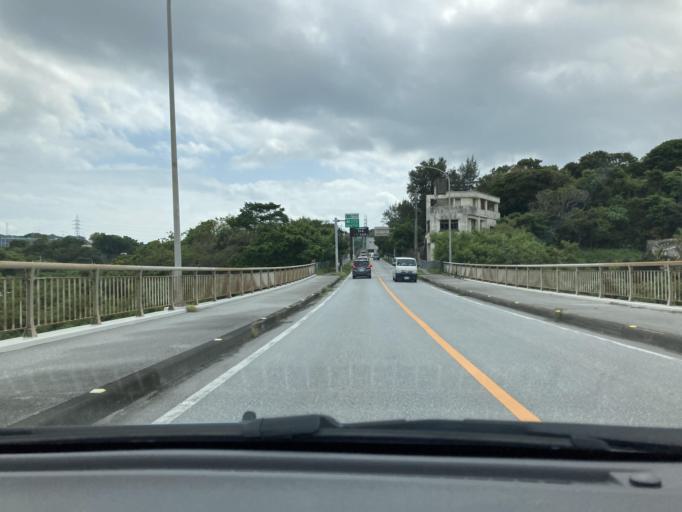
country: JP
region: Okinawa
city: Chatan
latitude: 26.2943
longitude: 127.7846
